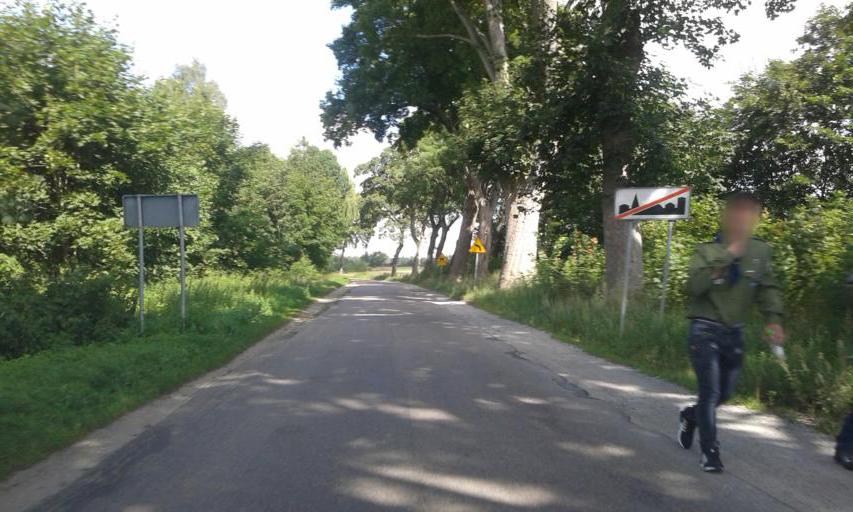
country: PL
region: West Pomeranian Voivodeship
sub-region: Powiat slawienski
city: Slawno
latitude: 54.3072
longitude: 16.6228
